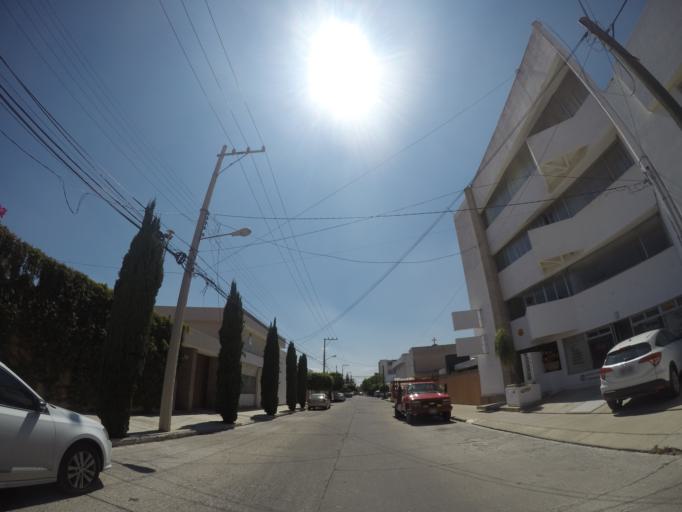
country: MX
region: San Luis Potosi
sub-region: San Luis Potosi
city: San Luis Potosi
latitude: 22.1423
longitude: -101.0067
